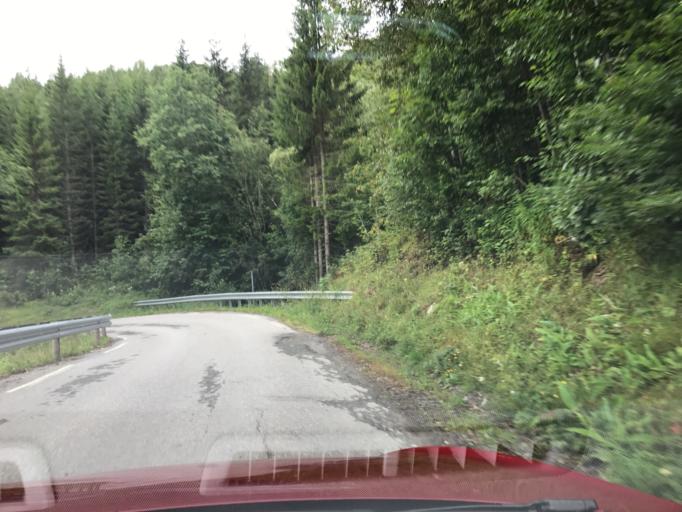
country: NO
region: Buskerud
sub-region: Rollag
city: Rollag
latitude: 60.0746
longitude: 9.1052
